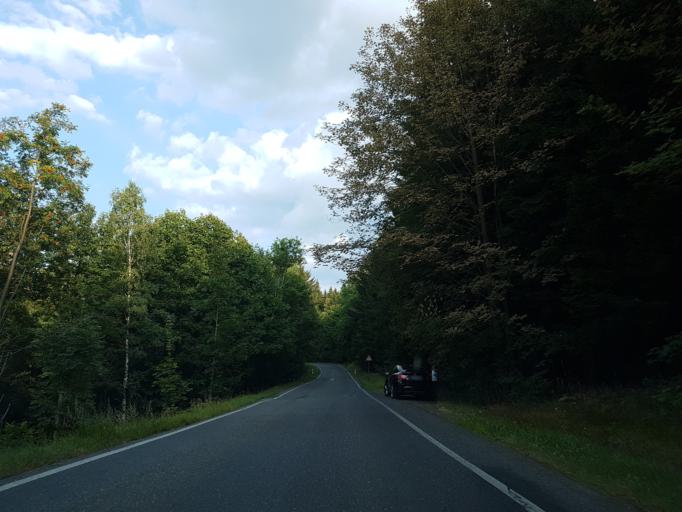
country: CZ
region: Liberecky
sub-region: Okres Jablonec nad Nisou
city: Jablonec nad Nisou
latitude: 50.7088
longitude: 15.1970
